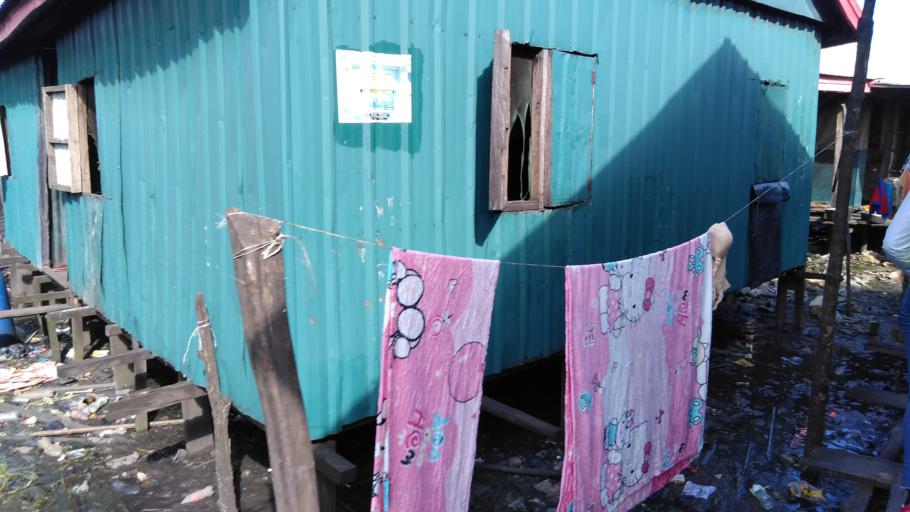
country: NG
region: Ondo
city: Igbekebo
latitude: 5.9216
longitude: 4.9689
